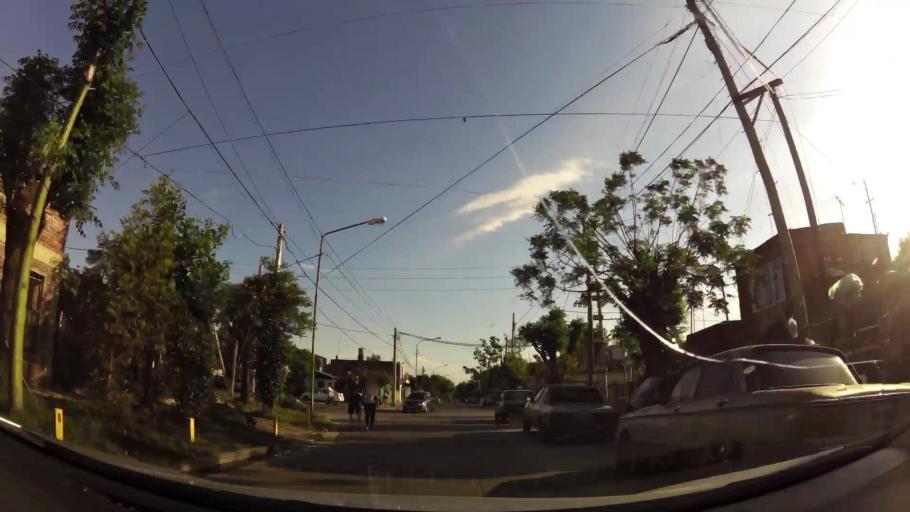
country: AR
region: Buenos Aires
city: Santa Catalina - Dique Lujan
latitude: -34.4636
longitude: -58.6648
